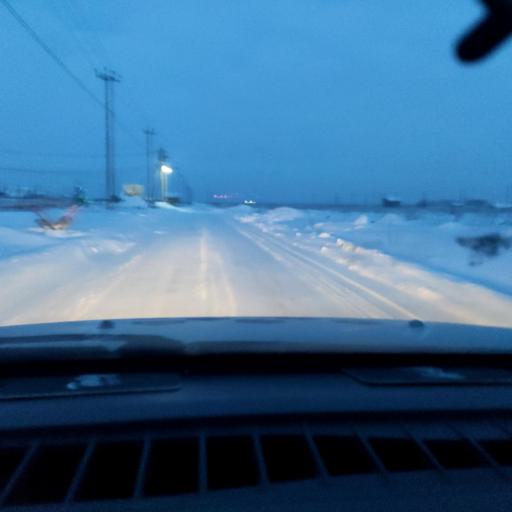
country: RU
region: Perm
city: Kultayevo
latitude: 57.8746
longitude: 55.9740
